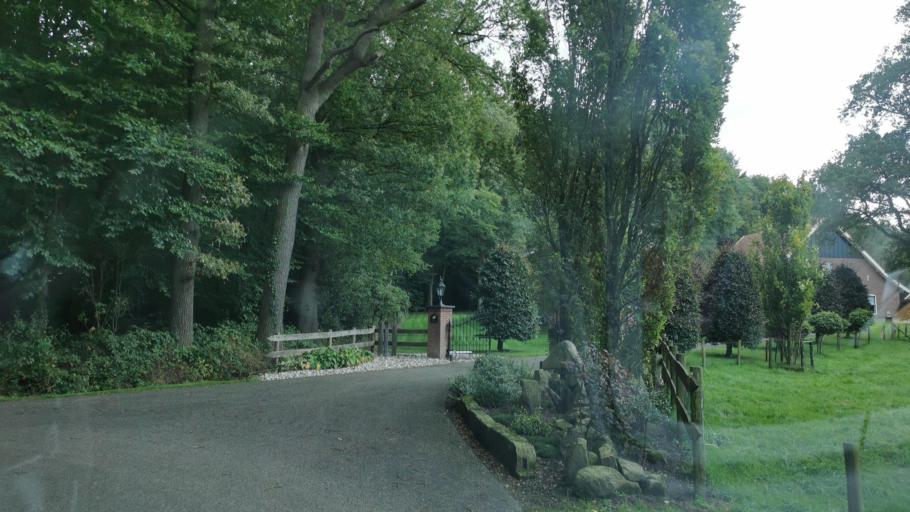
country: NL
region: Overijssel
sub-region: Gemeente Oldenzaal
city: Oldenzaal
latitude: 52.3347
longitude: 6.9835
